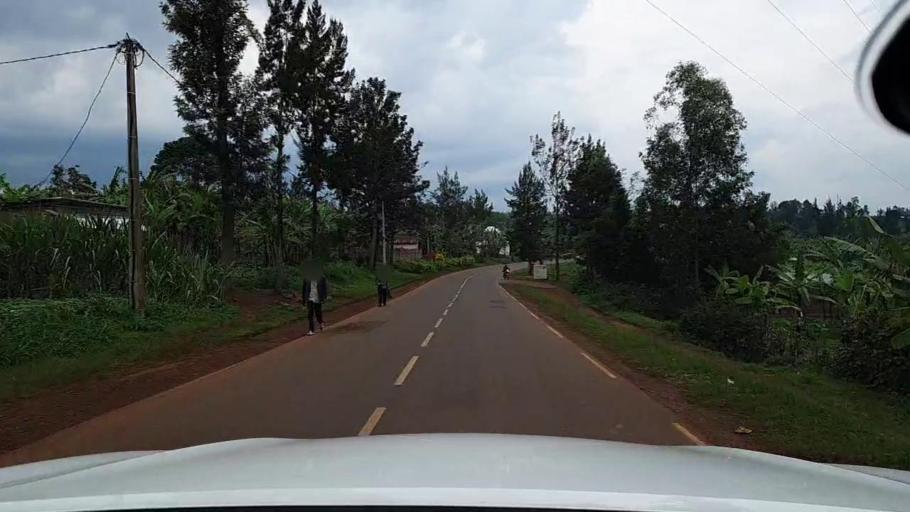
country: RW
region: Western Province
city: Cyangugu
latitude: -2.6137
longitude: 28.9420
